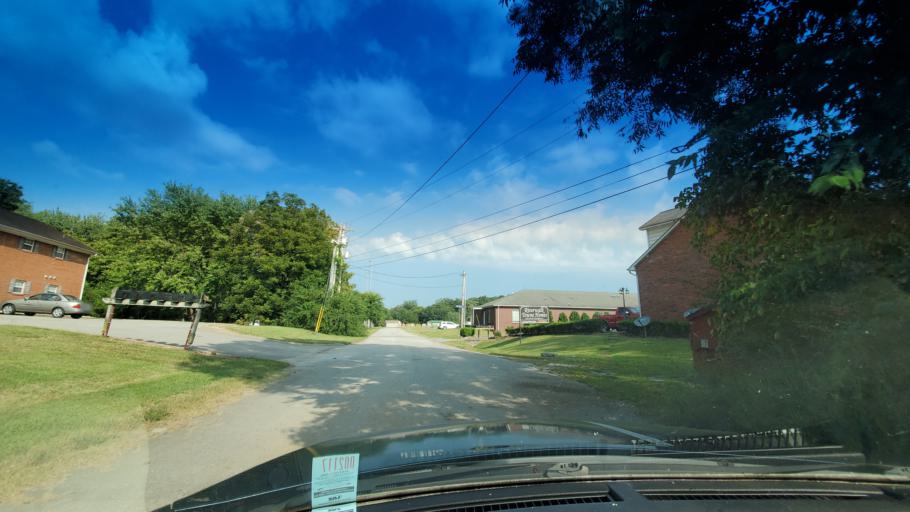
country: US
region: Tennessee
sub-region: Smith County
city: South Carthage
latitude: 36.2427
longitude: -85.9439
